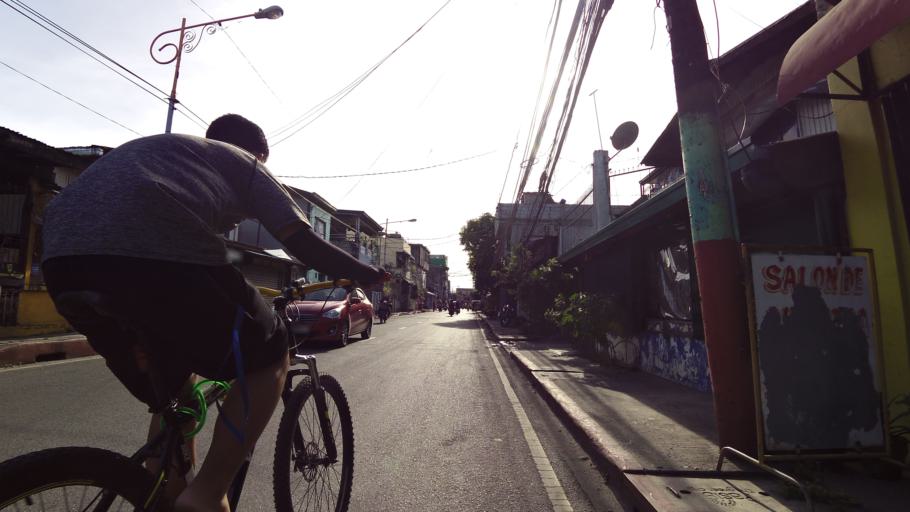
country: PH
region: Calabarzon
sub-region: Province of Rizal
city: Pateros
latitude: 14.5573
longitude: 121.0950
